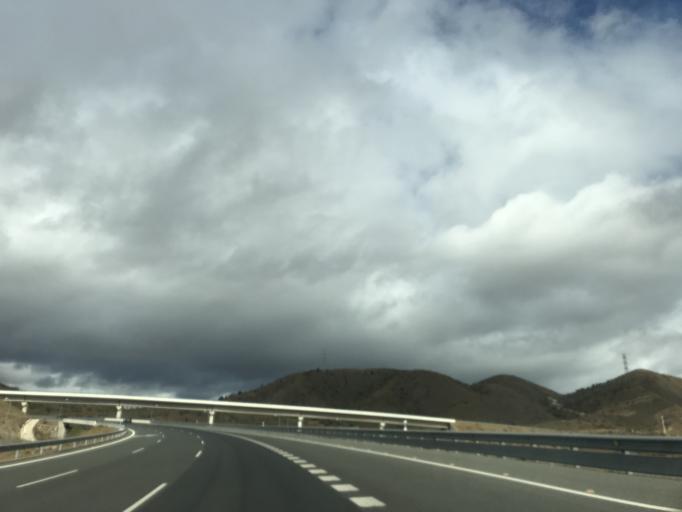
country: ES
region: Andalusia
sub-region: Provincia de Malaga
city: Malaga
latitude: 36.7545
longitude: -4.4841
